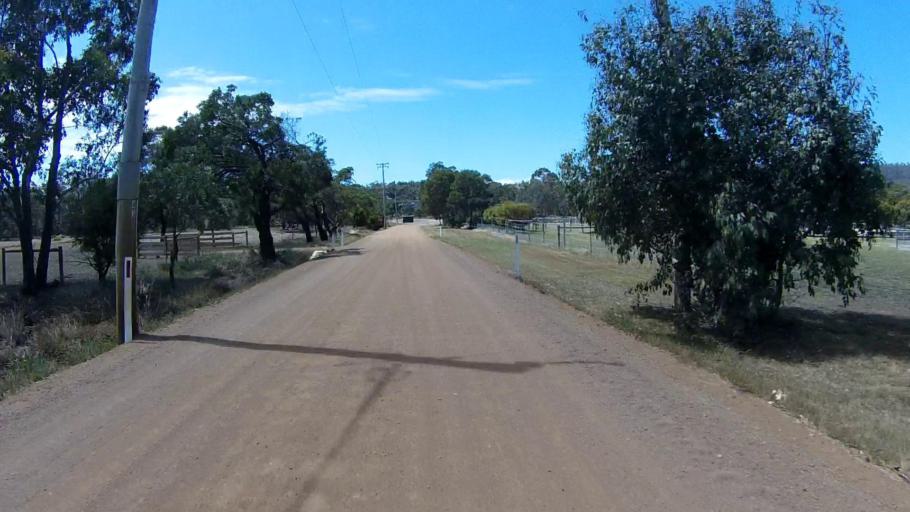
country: AU
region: Tasmania
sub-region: Clarence
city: Sandford
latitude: -42.9649
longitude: 147.4720
